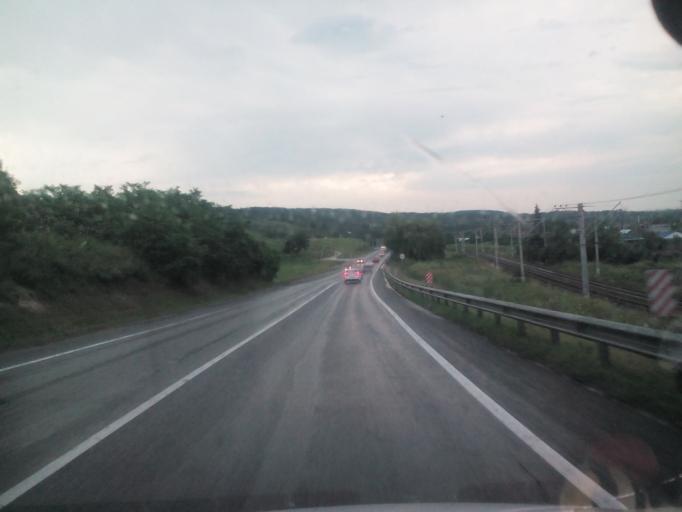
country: RU
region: Stavropol'skiy
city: Yasnaya Polyana
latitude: 43.9994
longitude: 42.7953
